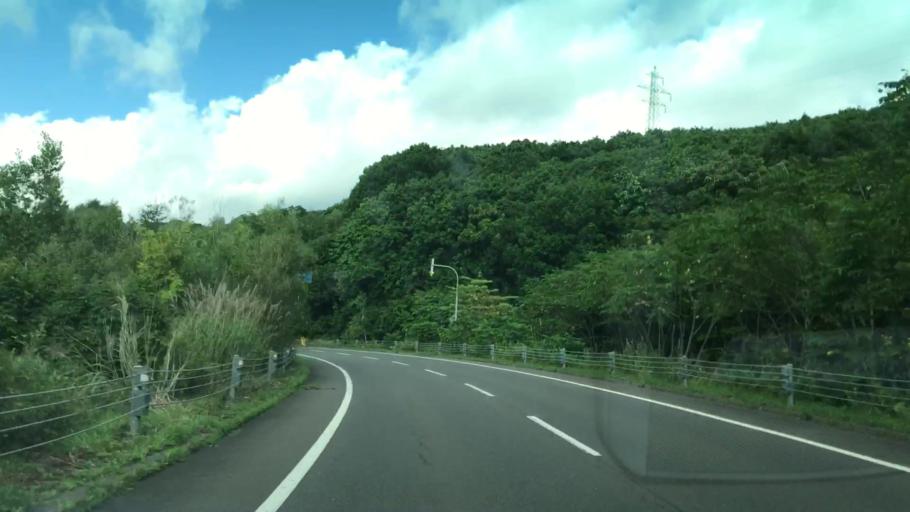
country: JP
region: Hokkaido
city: Muroran
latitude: 42.3719
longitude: 140.9603
